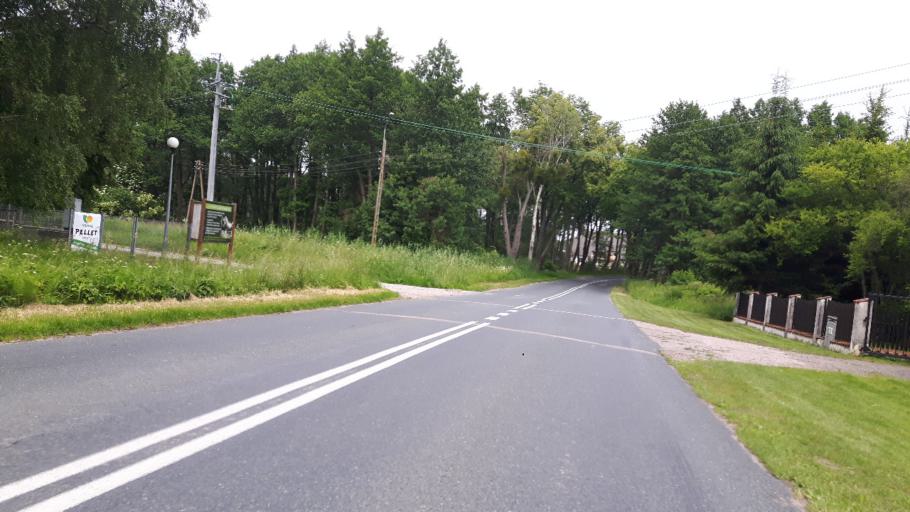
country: PL
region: Warmian-Masurian Voivodeship
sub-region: Powiat braniewski
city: Frombork
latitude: 54.3326
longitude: 19.6537
